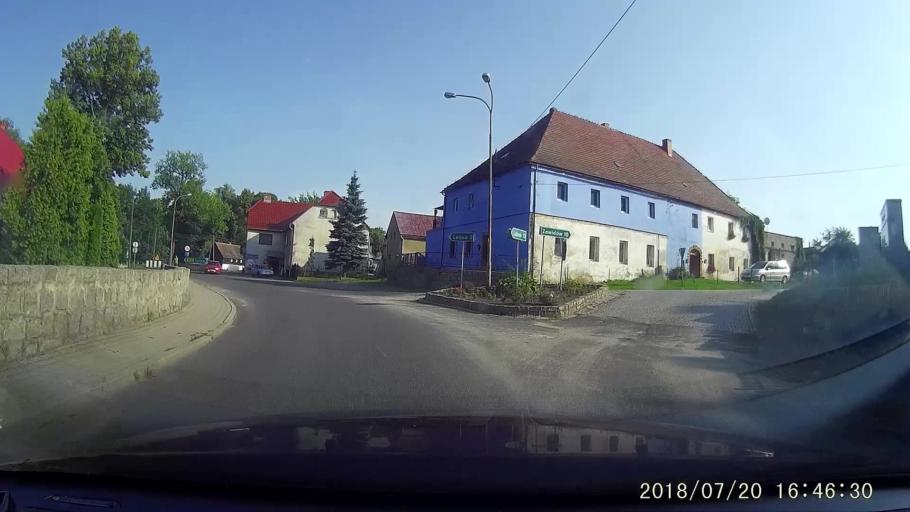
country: PL
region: Lower Silesian Voivodeship
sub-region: Powiat lubanski
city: Siekierczyn
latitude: 51.0615
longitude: 15.1708
